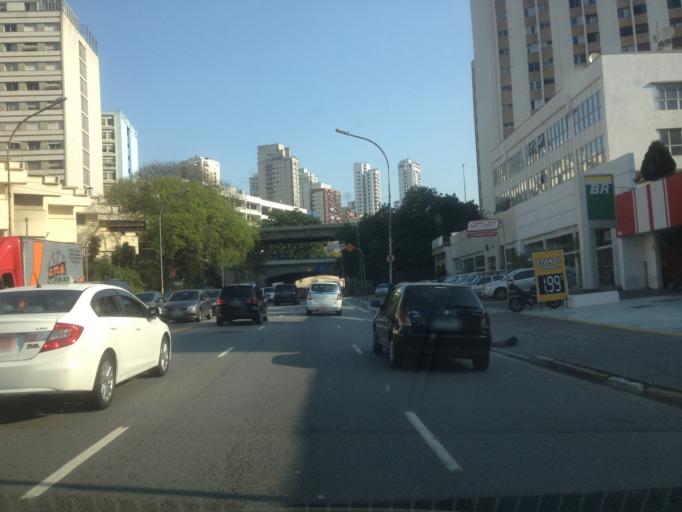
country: BR
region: Sao Paulo
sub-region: Sao Paulo
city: Sao Paulo
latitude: -23.5306
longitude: -46.6611
